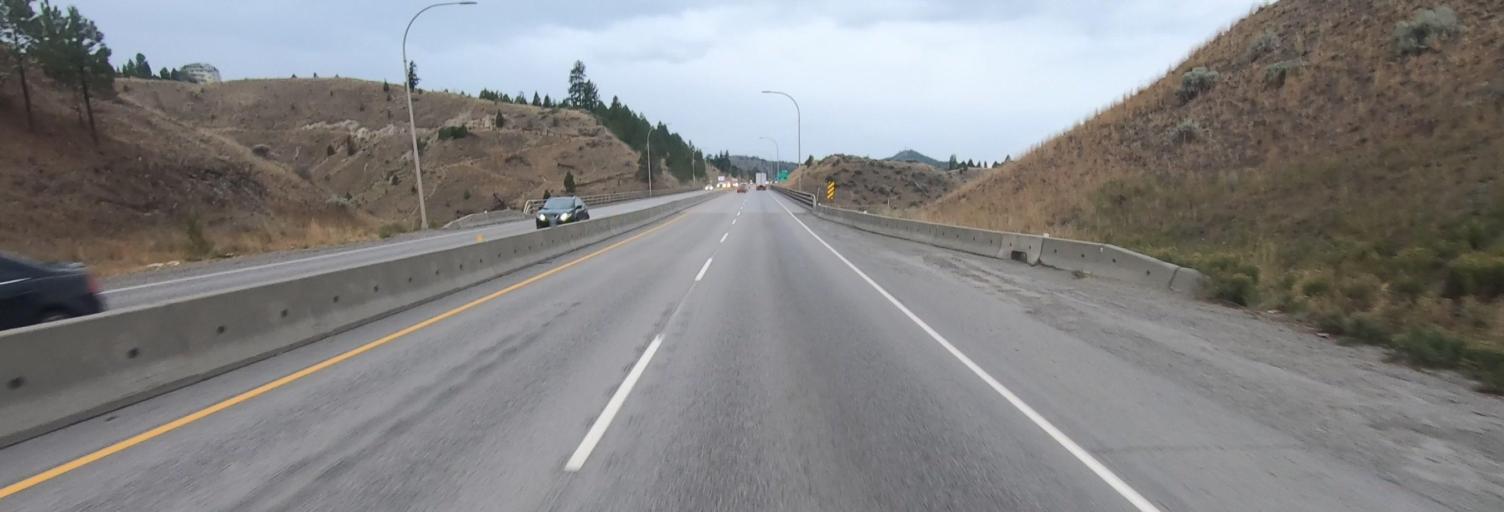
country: CA
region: British Columbia
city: Kamloops
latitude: 50.6619
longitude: -120.3276
